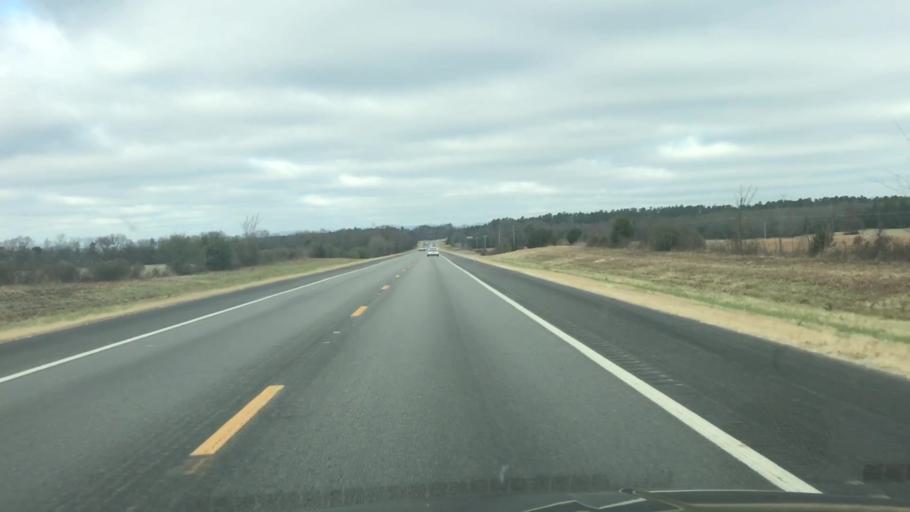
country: US
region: Arkansas
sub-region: Scott County
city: Waldron
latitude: 34.8764
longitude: -94.0934
